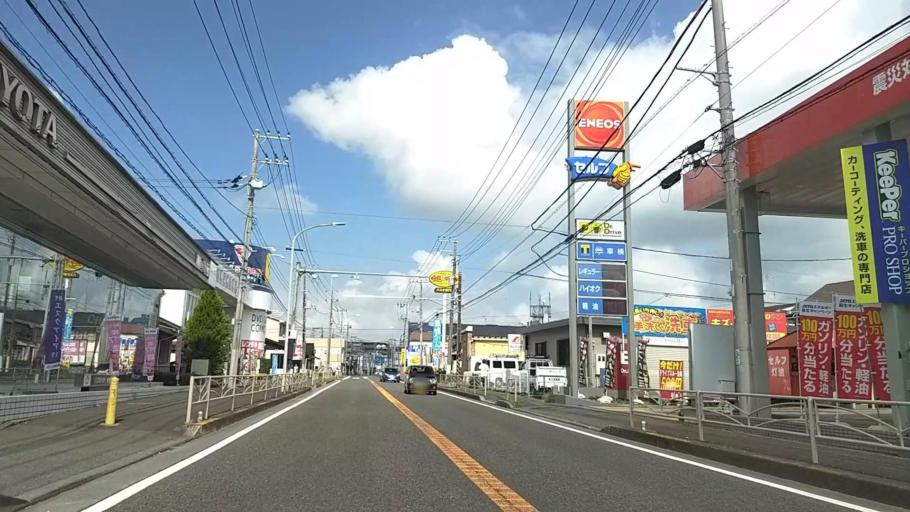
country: JP
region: Kanagawa
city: Minami-rinkan
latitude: 35.4834
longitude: 139.5274
